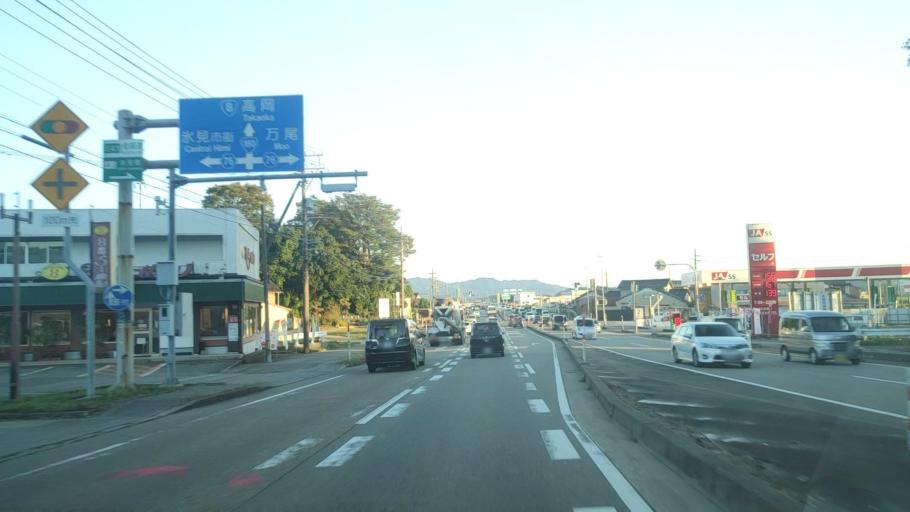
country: JP
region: Toyama
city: Himi
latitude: 36.8462
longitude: 136.9809
